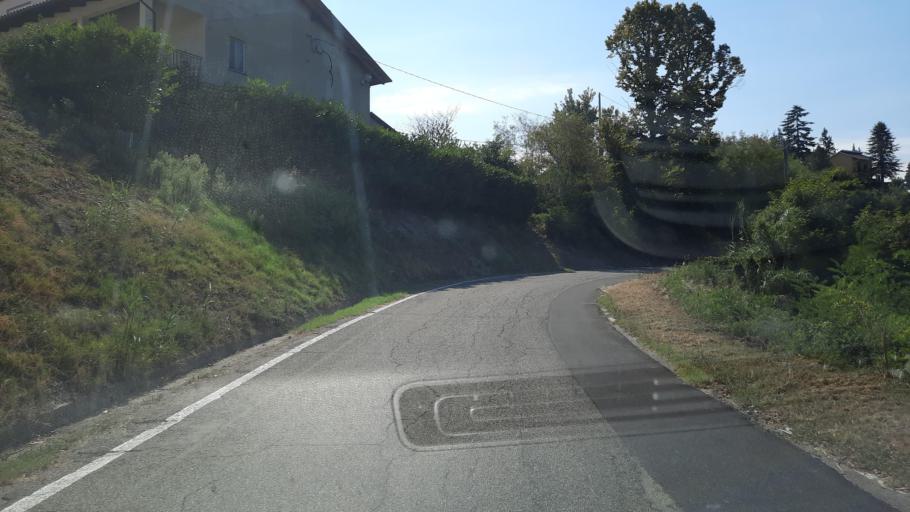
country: IT
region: Piedmont
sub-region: Provincia di Alessandria
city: Mombello Monferrato
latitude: 45.1547
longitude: 8.2409
